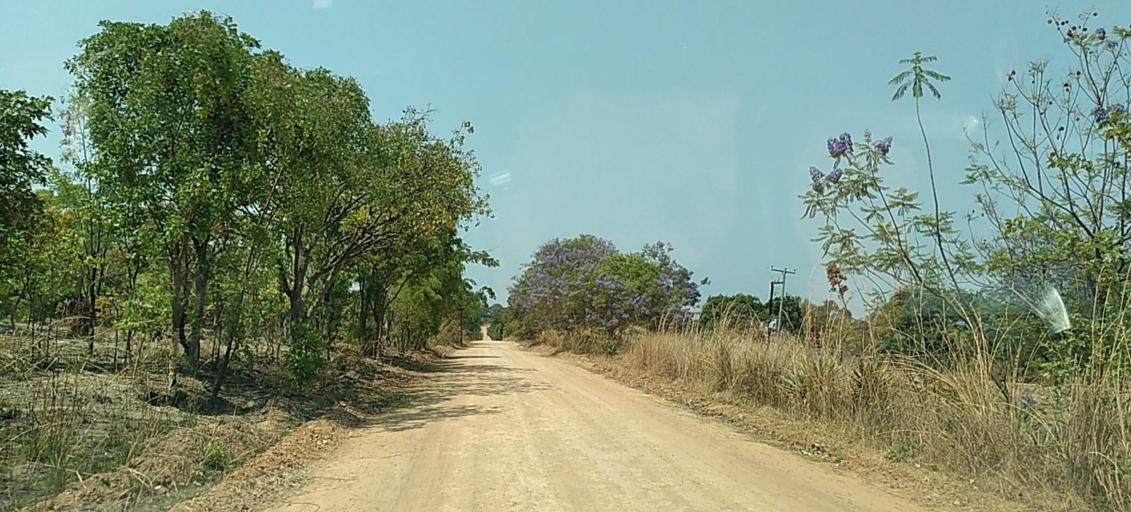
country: ZM
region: Copperbelt
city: Chambishi
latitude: -12.6156
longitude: 27.9568
